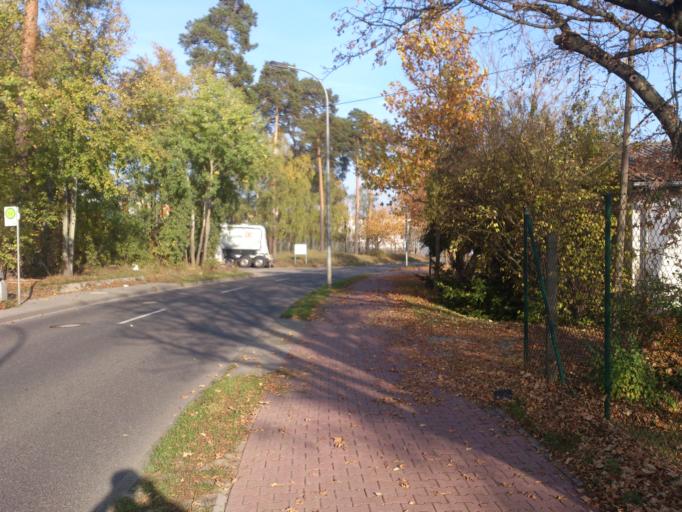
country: DE
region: Brandenburg
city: Ludwigsfelde
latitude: 52.3272
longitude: 13.2612
